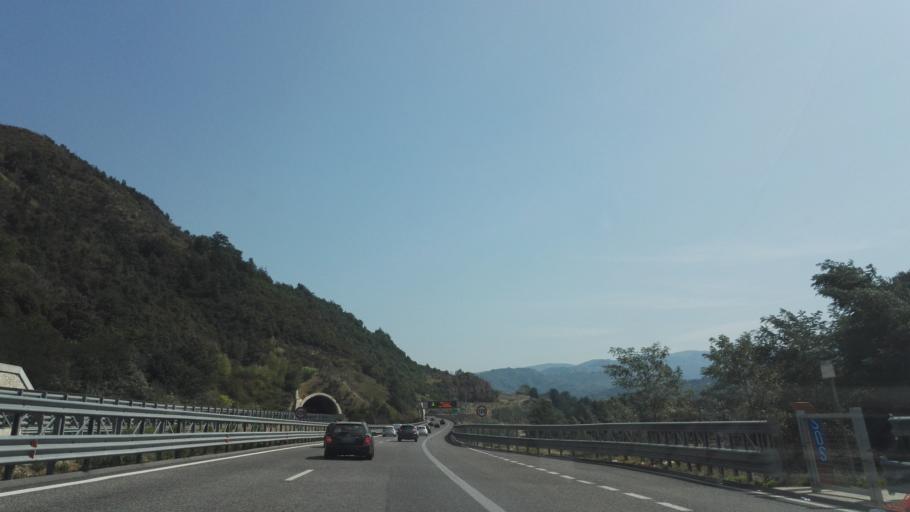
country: IT
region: Calabria
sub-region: Provincia di Catanzaro
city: Martirano
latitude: 39.0952
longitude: 16.2351
